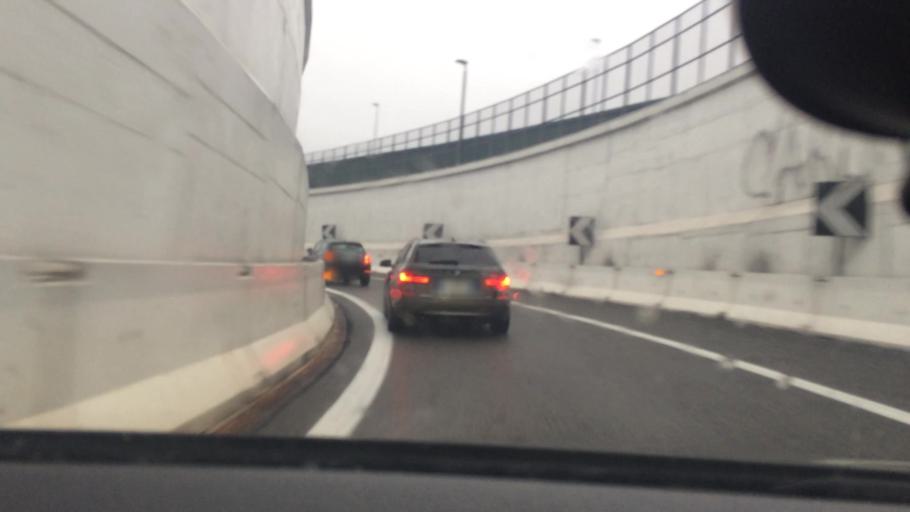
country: IT
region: Lombardy
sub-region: Citta metropolitana di Milano
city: Pero
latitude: 45.5138
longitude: 9.0846
